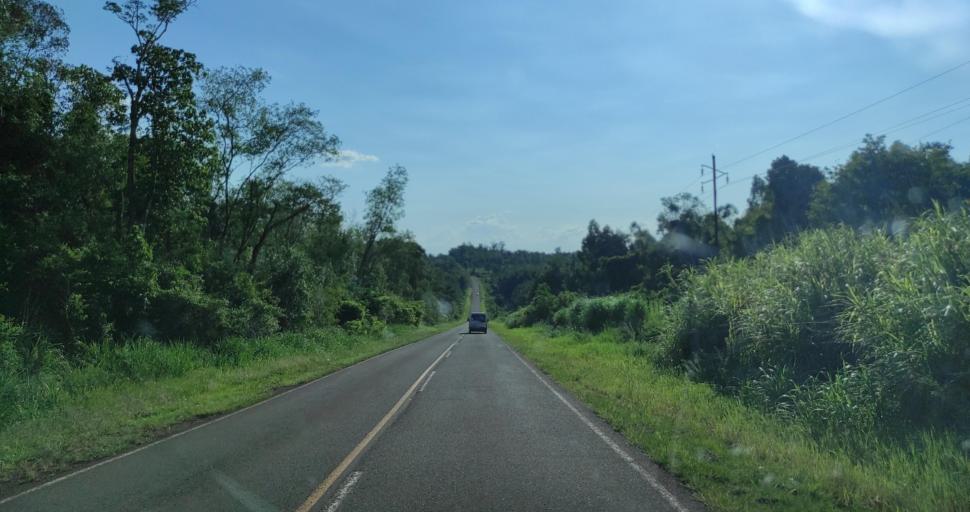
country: AR
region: Misiones
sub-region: Departamento de Eldorado
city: Eldorado
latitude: -26.3854
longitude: -54.3464
